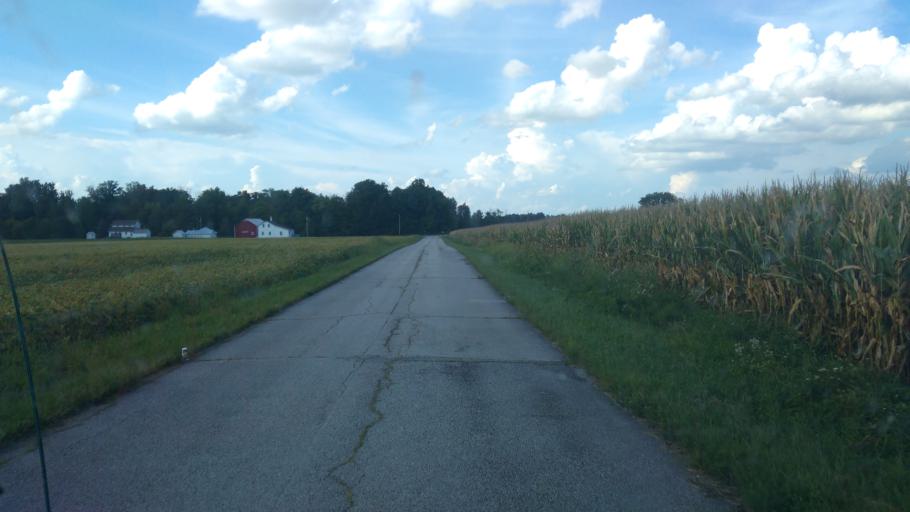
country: US
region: Ohio
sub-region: Crawford County
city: Galion
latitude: 40.7671
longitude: -82.7749
